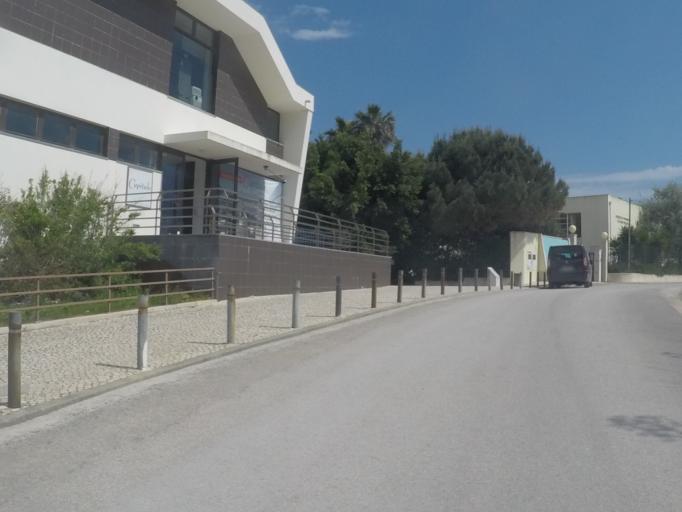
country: PT
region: Setubal
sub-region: Sesimbra
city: Sesimbra
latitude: 38.4355
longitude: -9.1153
